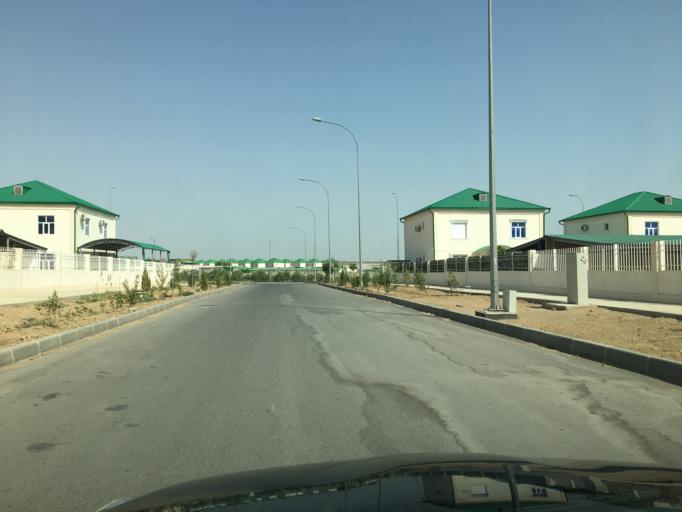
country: TM
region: Ahal
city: Ashgabat
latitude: 38.0050
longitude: 58.3956
